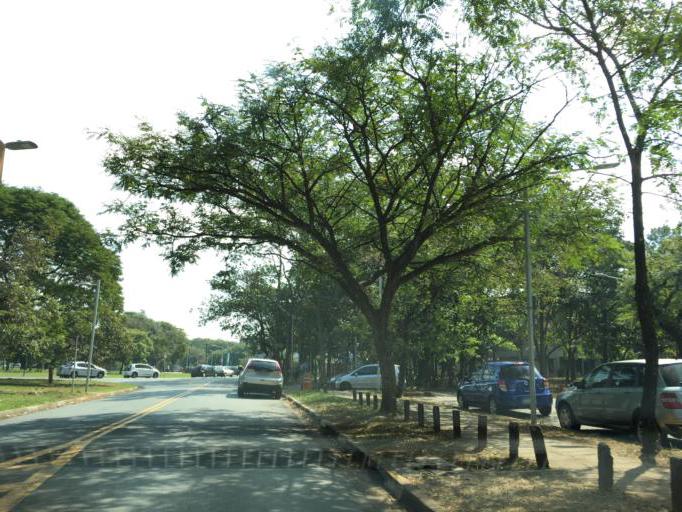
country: BR
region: Sao Paulo
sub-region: Osasco
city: Osasco
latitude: -23.5605
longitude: -46.7307
